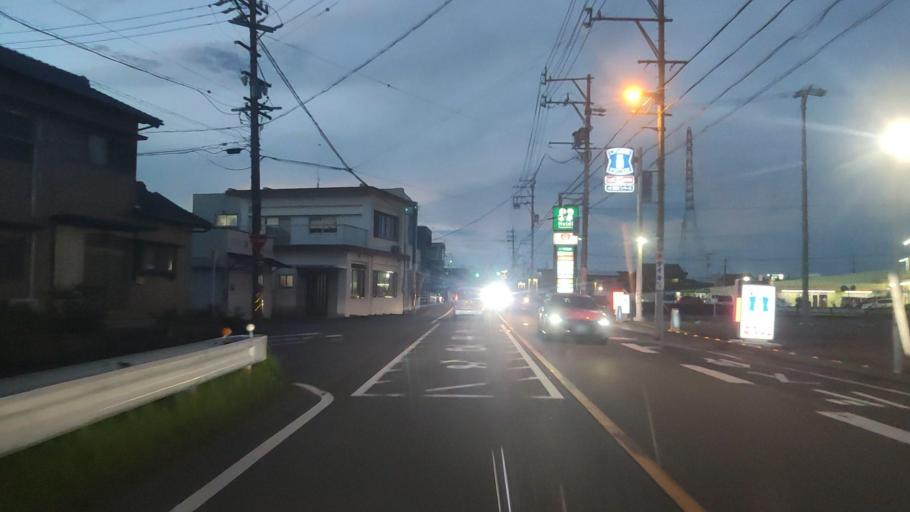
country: JP
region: Mie
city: Ise
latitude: 34.5044
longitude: 136.7177
